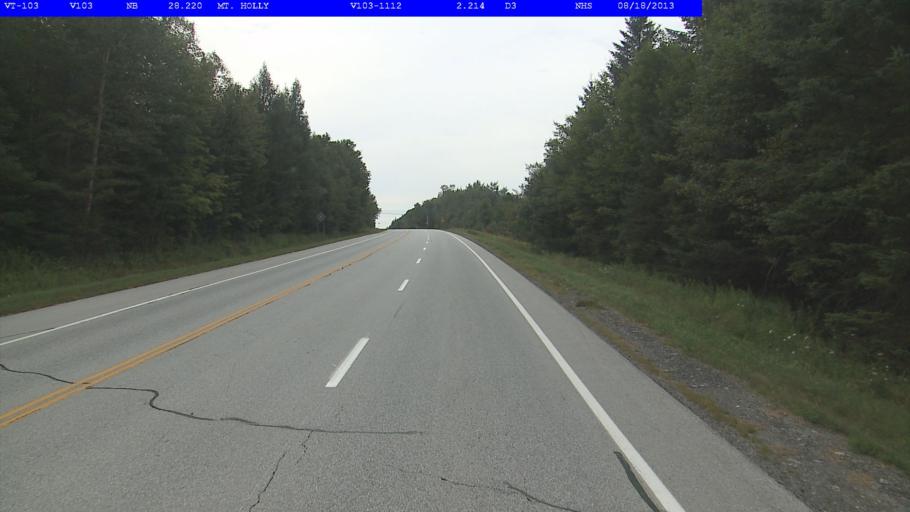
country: US
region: Vermont
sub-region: Windsor County
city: Chester
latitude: 43.4457
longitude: -72.7724
